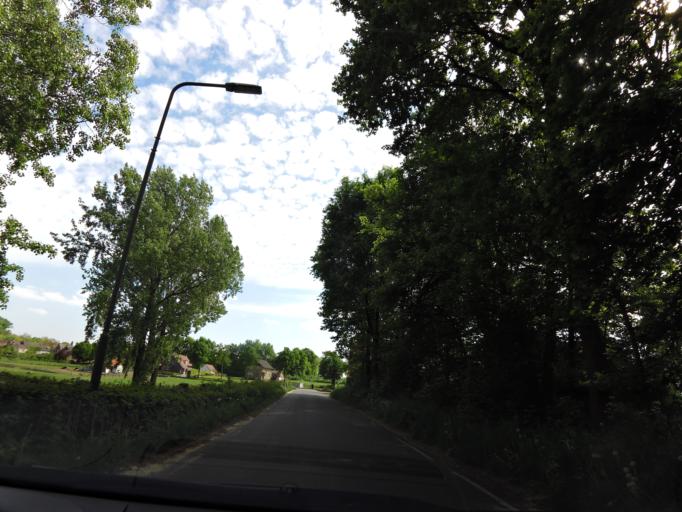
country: NL
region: Limburg
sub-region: Gemeente Roermond
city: Roermond
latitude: 51.1696
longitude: 5.9853
